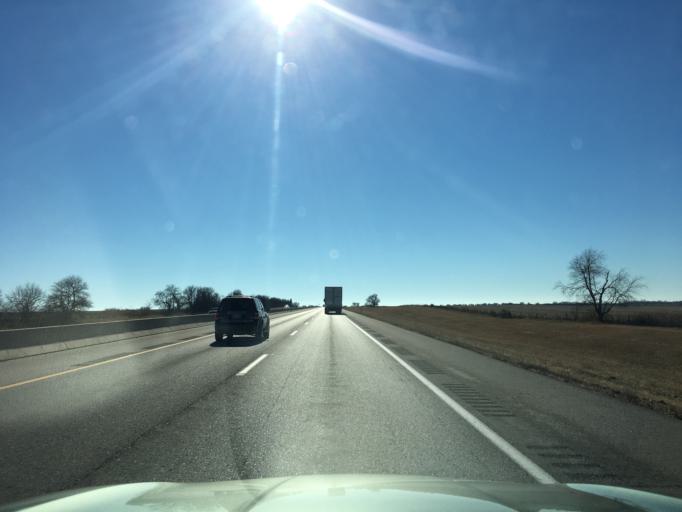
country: US
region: Kansas
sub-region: Sumner County
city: Wellington
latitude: 37.1130
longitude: -97.3388
